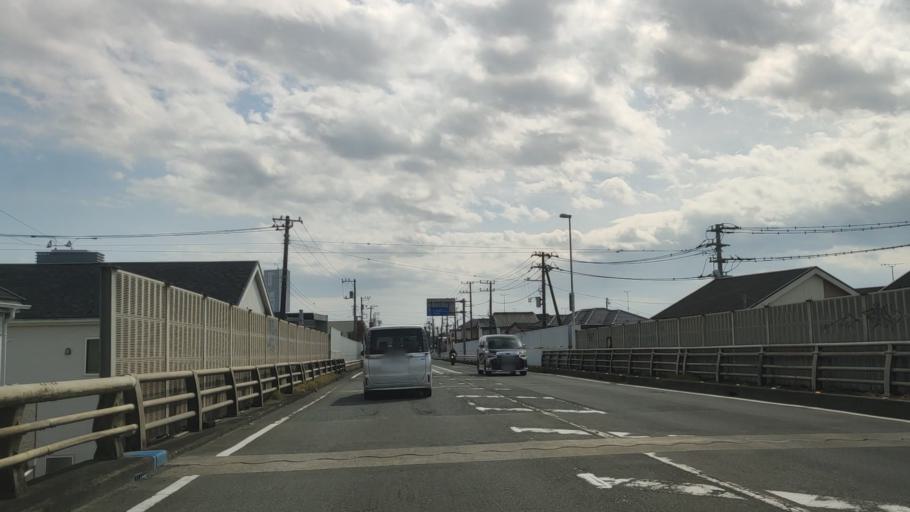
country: JP
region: Kanagawa
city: Hadano
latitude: 35.3447
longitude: 139.1475
